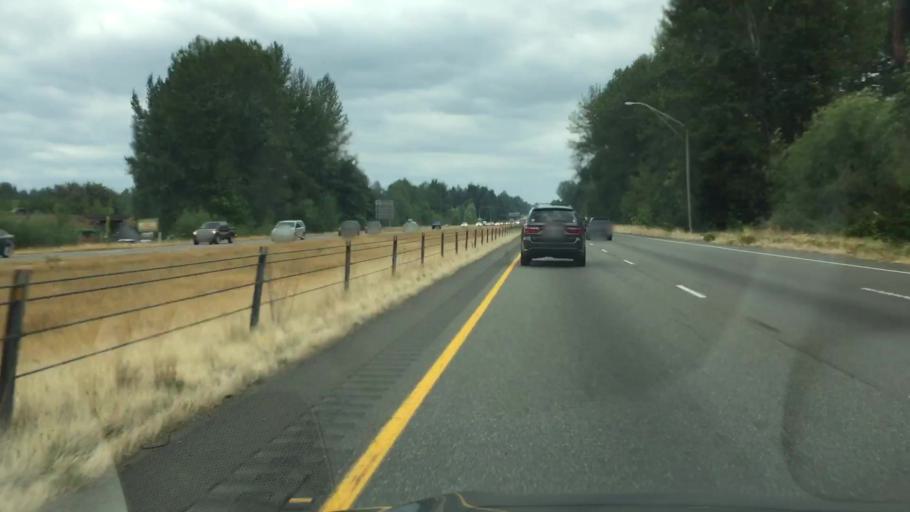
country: US
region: Washington
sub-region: Pierce County
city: Puyallup
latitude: 47.1591
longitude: -122.3055
